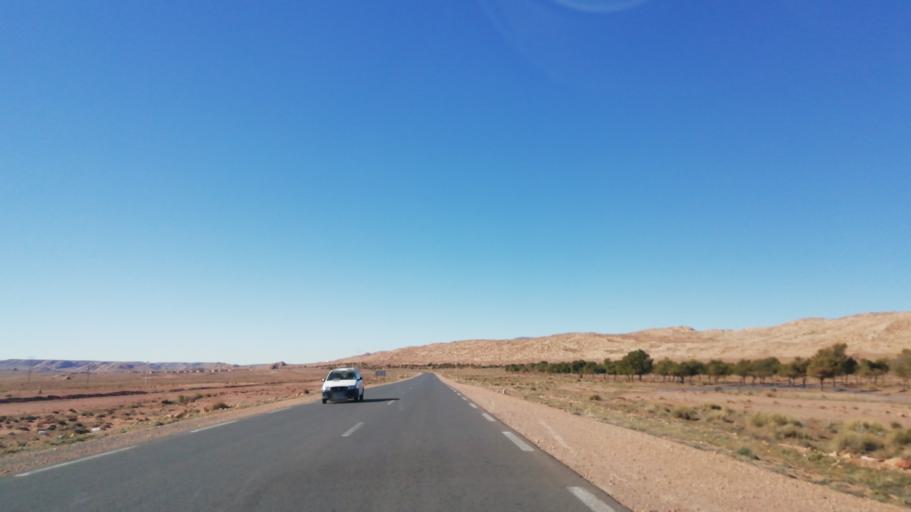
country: DZ
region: El Bayadh
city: El Bayadh
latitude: 33.6176
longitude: 1.1930
